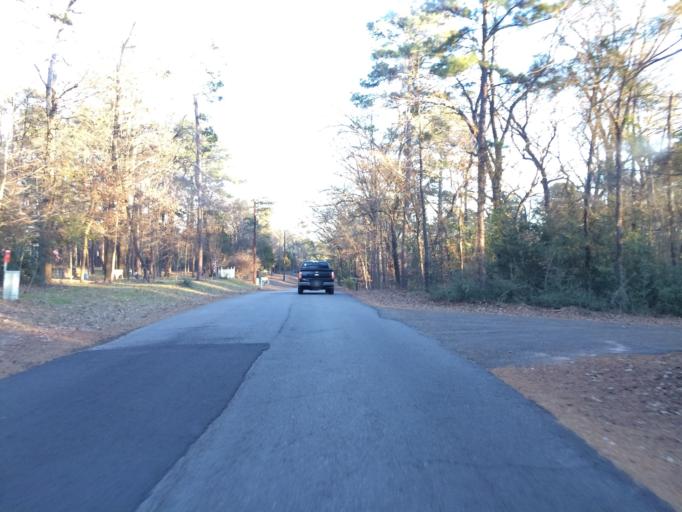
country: US
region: Texas
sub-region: Wood County
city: Hawkins
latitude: 32.7245
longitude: -95.1790
